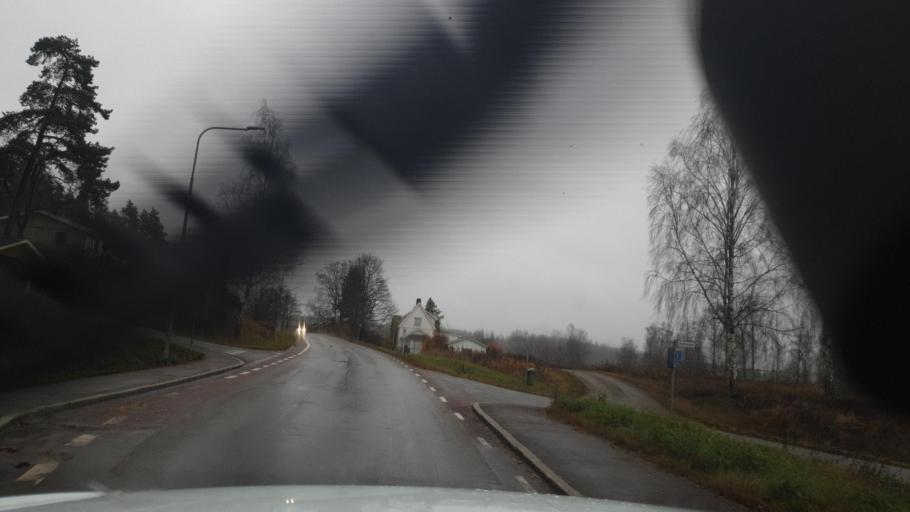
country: SE
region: Vaermland
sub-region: Arvika Kommun
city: Arvika
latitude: 59.6259
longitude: 12.8329
